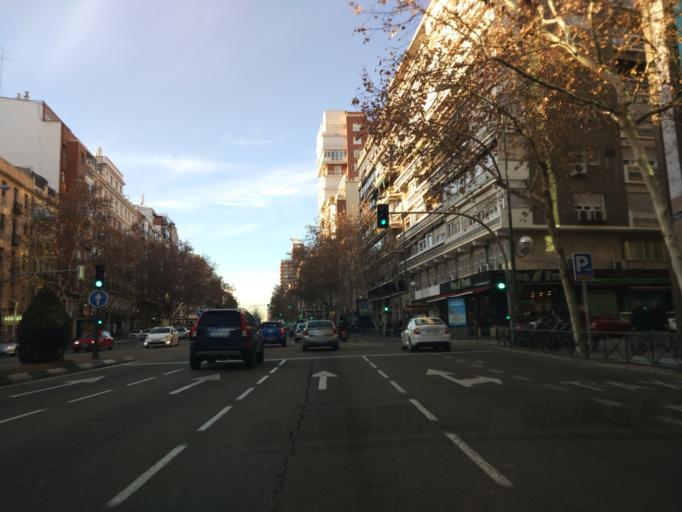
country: ES
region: Madrid
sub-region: Provincia de Madrid
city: Salamanca
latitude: 40.4333
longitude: -3.6731
